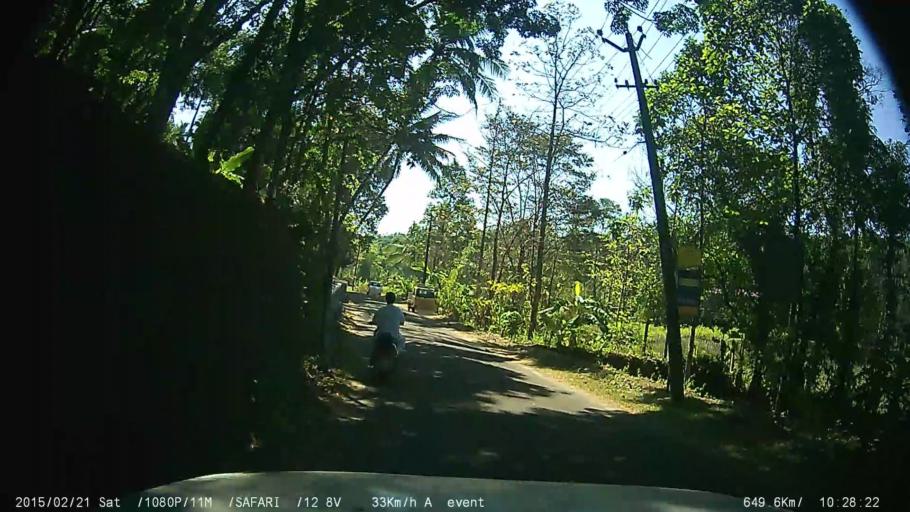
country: IN
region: Kerala
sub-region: Kottayam
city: Palackattumala
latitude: 9.8560
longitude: 76.6924
